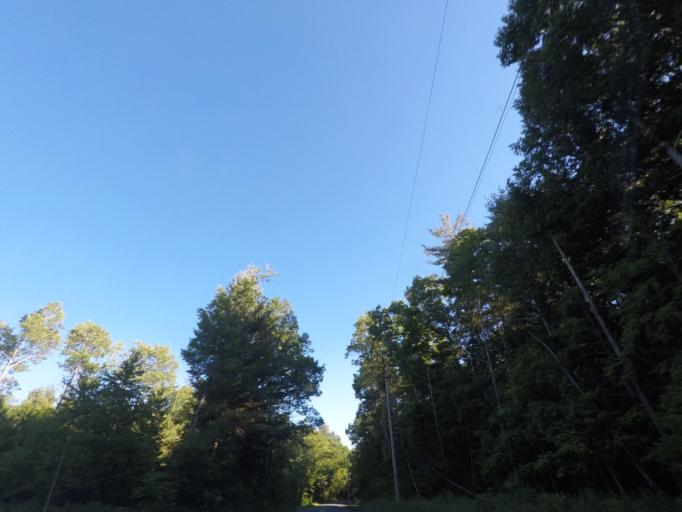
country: US
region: New York
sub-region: Rensselaer County
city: Averill Park
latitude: 42.5637
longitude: -73.5317
